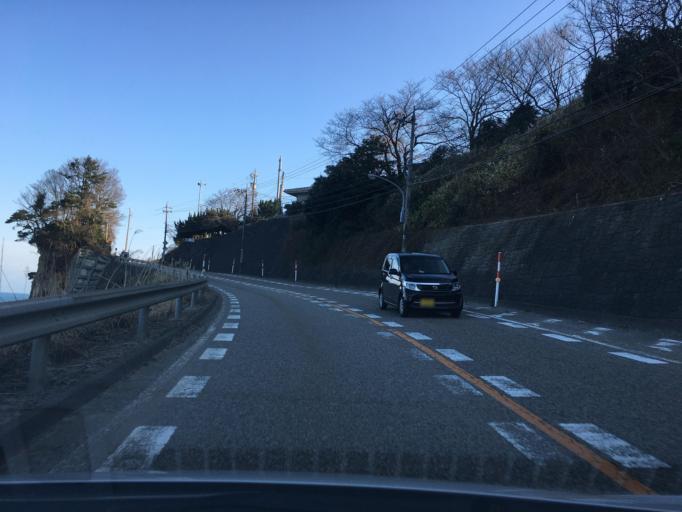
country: JP
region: Ishikawa
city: Nanao
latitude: 36.9839
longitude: 137.0490
